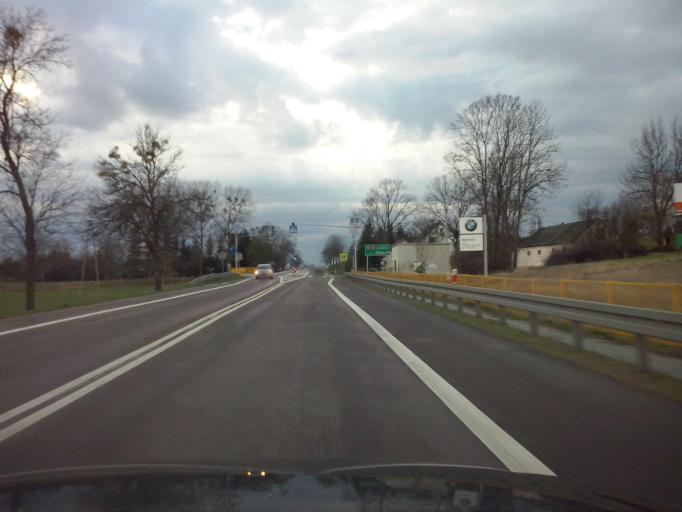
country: PL
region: Lublin Voivodeship
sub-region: Chelm
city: Chelm
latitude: 51.1628
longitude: 23.3879
